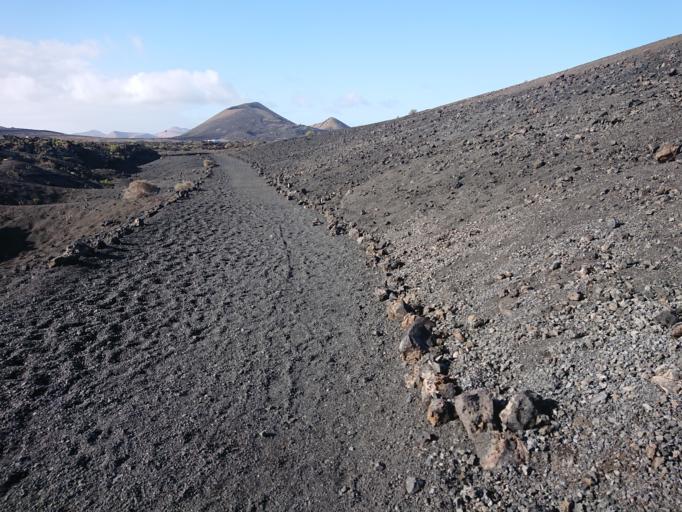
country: ES
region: Canary Islands
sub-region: Provincia de Las Palmas
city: Tias
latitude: 28.9895
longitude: -13.6935
